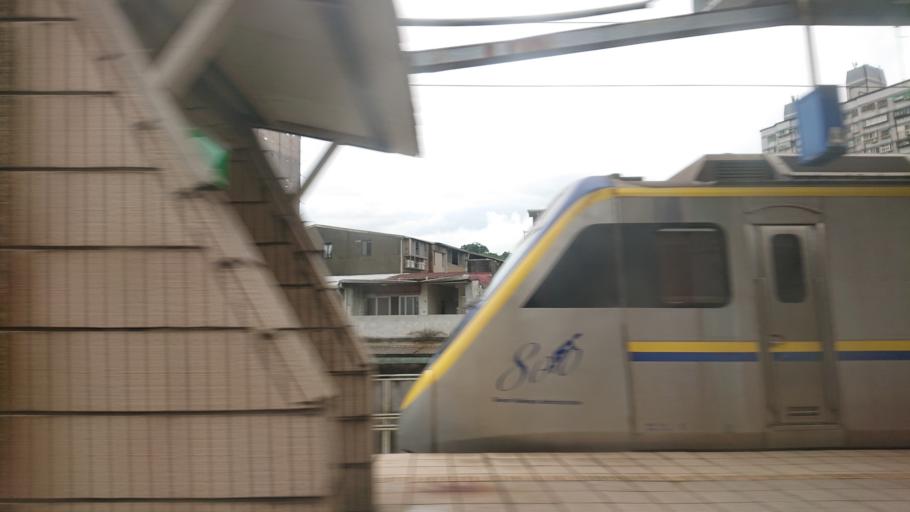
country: TW
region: Taiwan
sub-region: Keelung
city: Keelung
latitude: 25.0784
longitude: 121.6683
